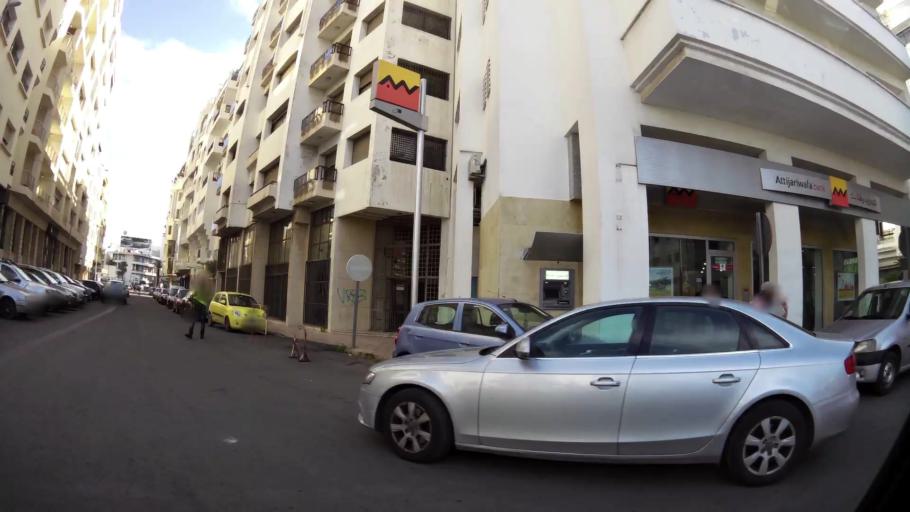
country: MA
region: Grand Casablanca
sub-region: Casablanca
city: Casablanca
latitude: 33.5896
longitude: -7.6365
